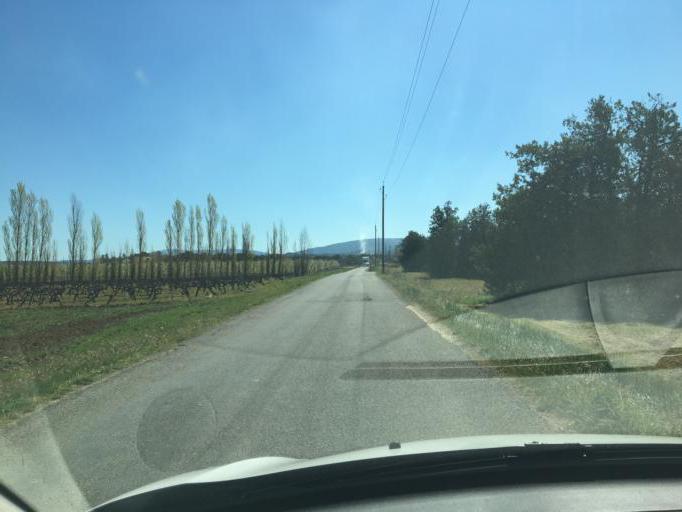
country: FR
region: Provence-Alpes-Cote d'Azur
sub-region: Departement du Vaucluse
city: Robion
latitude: 43.8637
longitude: 5.1256
